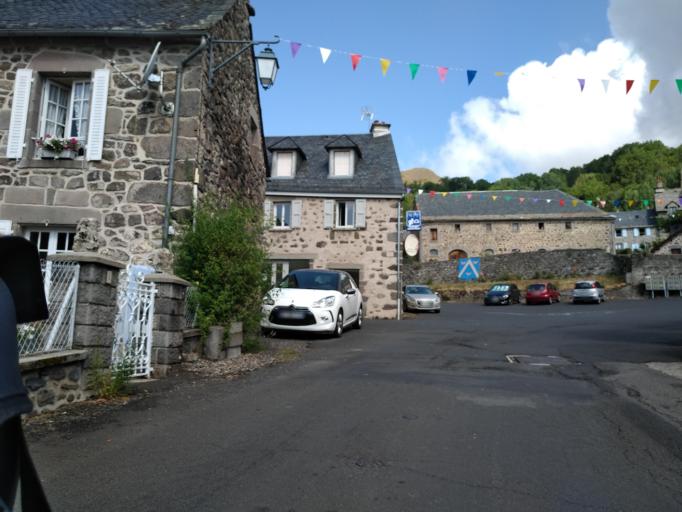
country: FR
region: Auvergne
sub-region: Departement du Cantal
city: Murat
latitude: 45.1584
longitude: 2.7872
